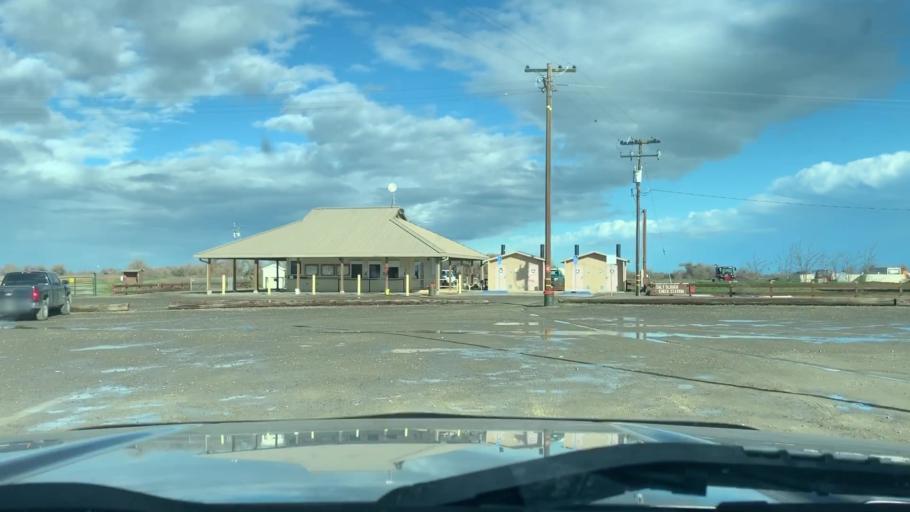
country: US
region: California
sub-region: Merced County
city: Los Banos
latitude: 37.1590
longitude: -120.8137
